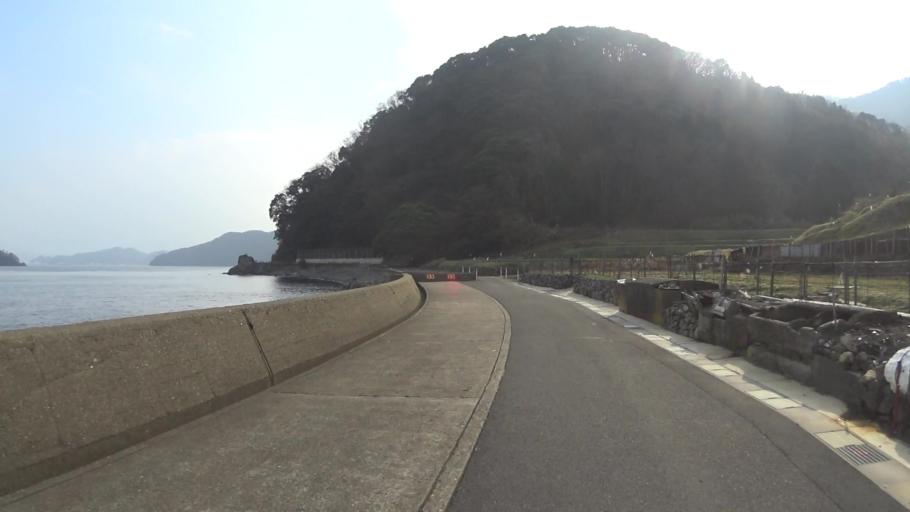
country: JP
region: Kyoto
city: Maizuru
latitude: 35.5100
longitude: 135.3315
